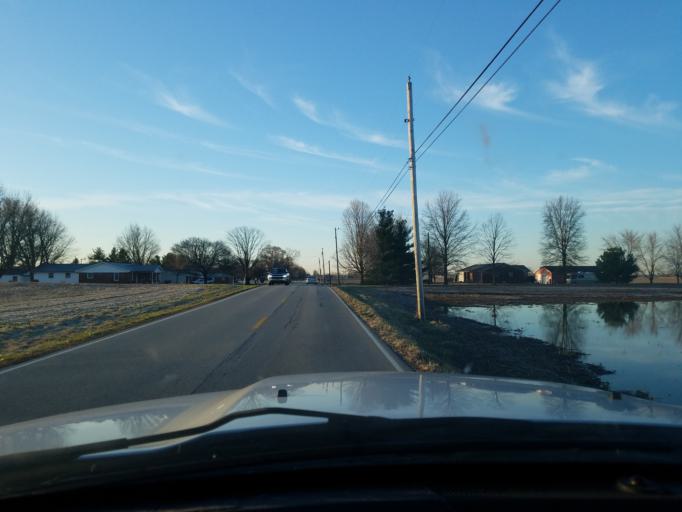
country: US
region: Indiana
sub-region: Johnson County
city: Whiteland
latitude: 39.5428
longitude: -86.0593
